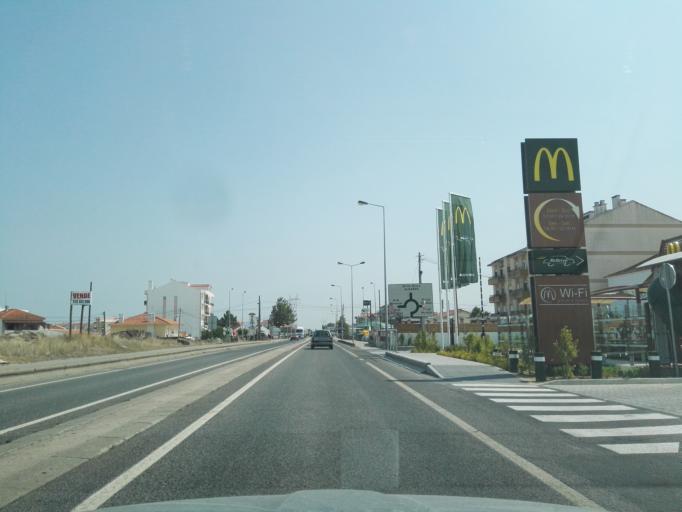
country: PT
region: Santarem
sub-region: Benavente
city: Samora Correia
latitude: 38.9227
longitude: -8.8851
